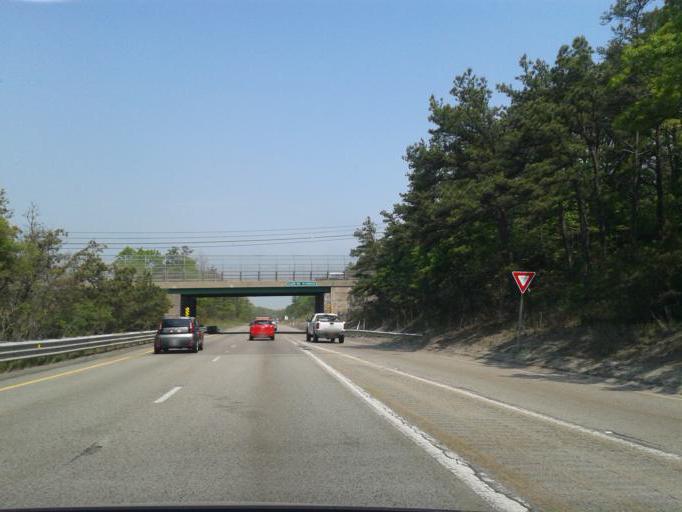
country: US
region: Massachusetts
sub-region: Plymouth County
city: White Island Shores
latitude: 41.8731
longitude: -70.6007
